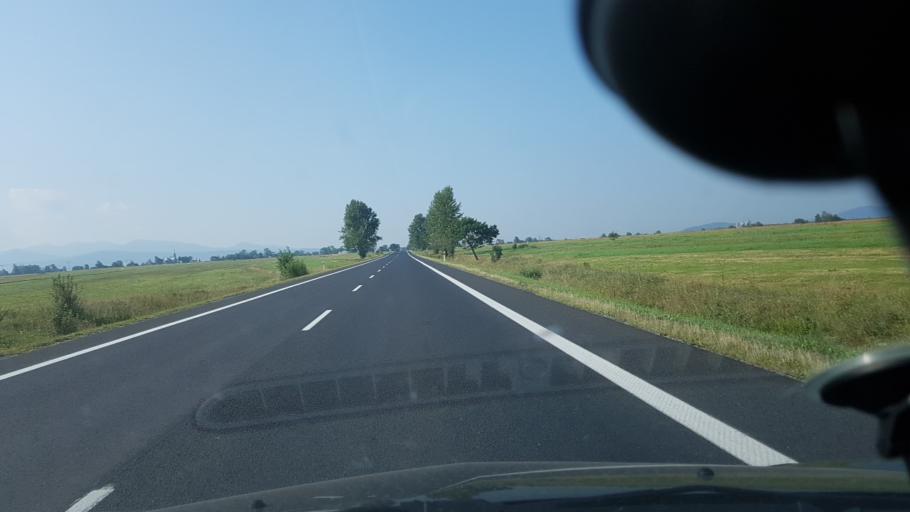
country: PL
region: Lesser Poland Voivodeship
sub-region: Powiat nowotarski
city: Chyzne
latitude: 49.4373
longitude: 19.6803
